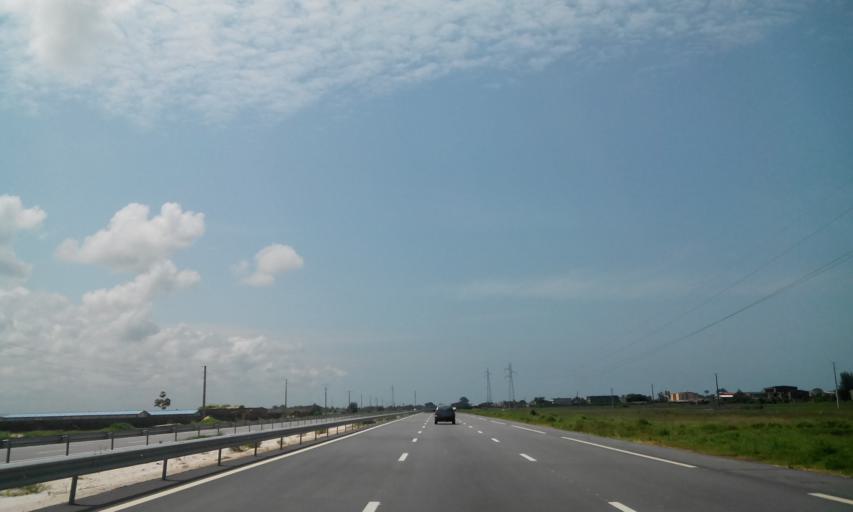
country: CI
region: Sud-Comoe
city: Grand-Bassam
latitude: 5.2278
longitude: -3.7444
